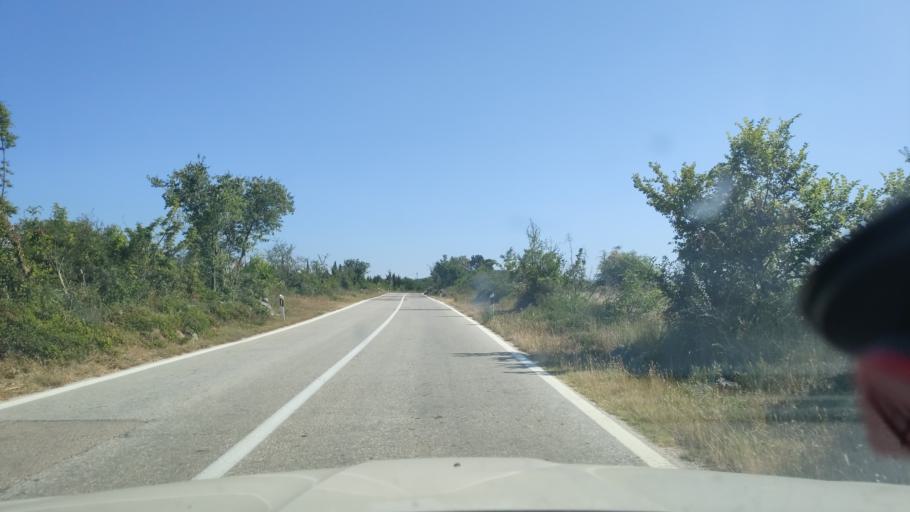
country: HR
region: Sibensko-Kniniska
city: Kistanje
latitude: 43.9593
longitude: 15.8634
